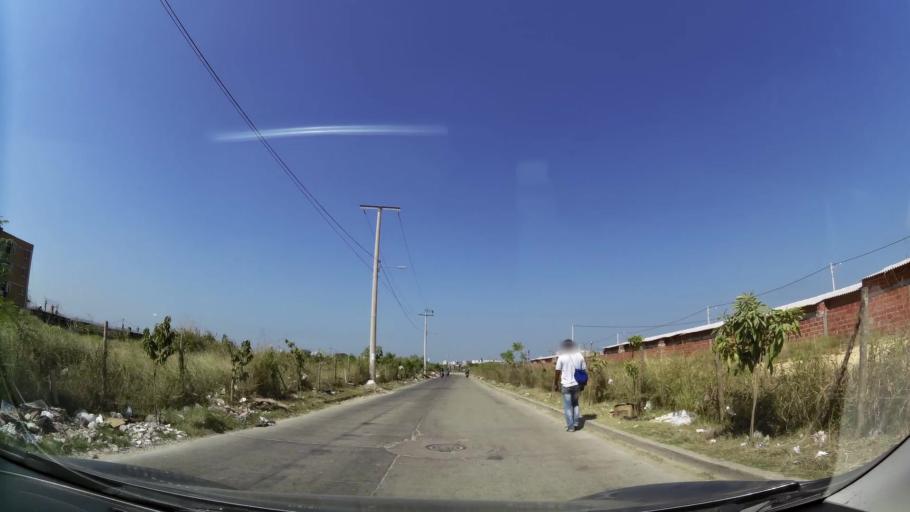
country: CO
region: Bolivar
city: Cartagena
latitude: 10.3919
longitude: -75.4501
